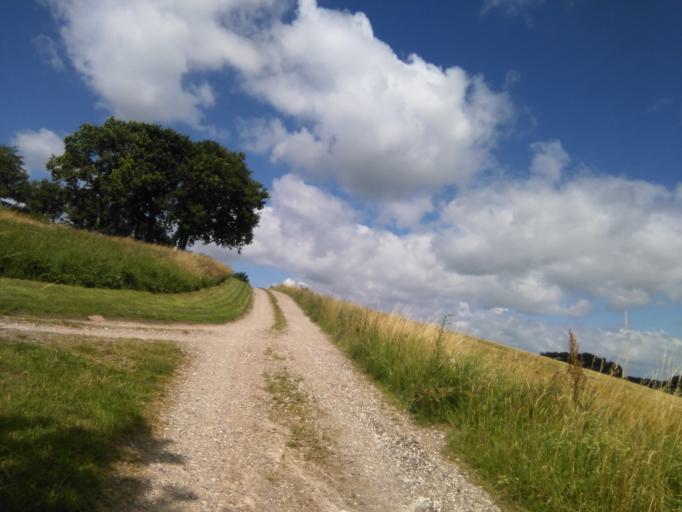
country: DK
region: Central Jutland
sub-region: Arhus Kommune
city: Logten
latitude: 56.1659
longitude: 10.3973
